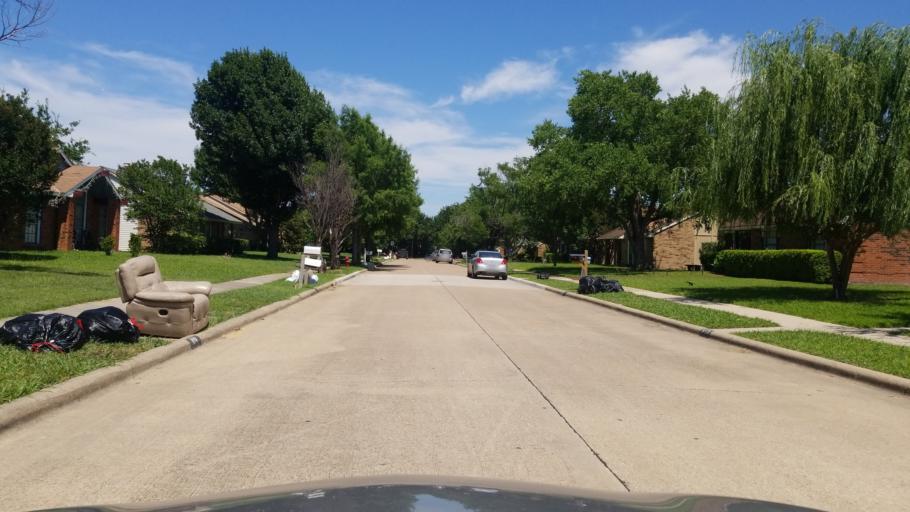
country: US
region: Texas
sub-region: Dallas County
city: Grand Prairie
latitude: 32.6855
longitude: -97.0008
